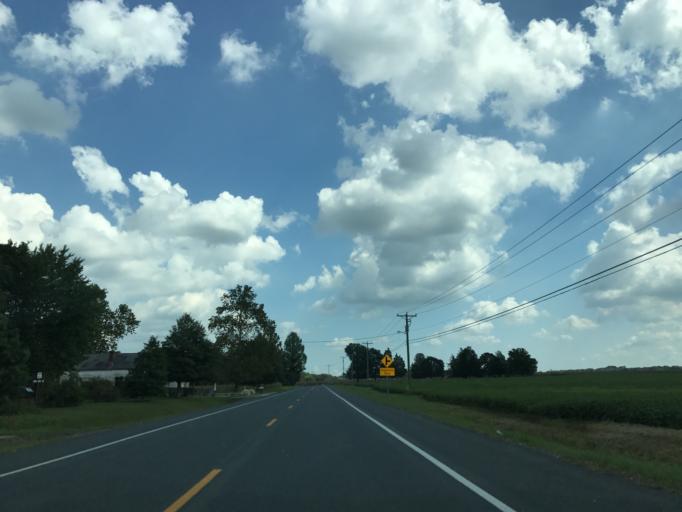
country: US
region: Maryland
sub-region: Caroline County
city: Greensboro
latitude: 39.1343
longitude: -75.7787
